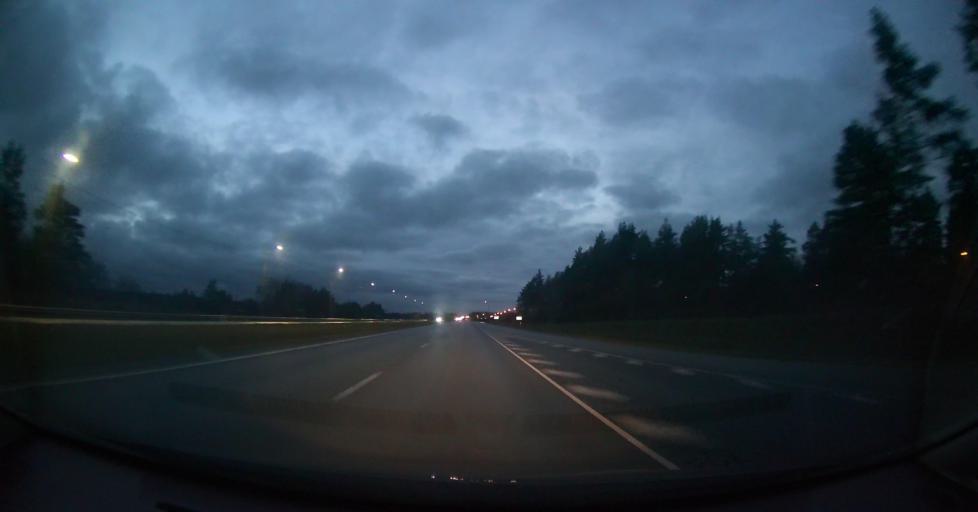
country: EE
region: Harju
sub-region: Kuusalu vald
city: Kuusalu
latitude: 59.4478
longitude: 25.4174
